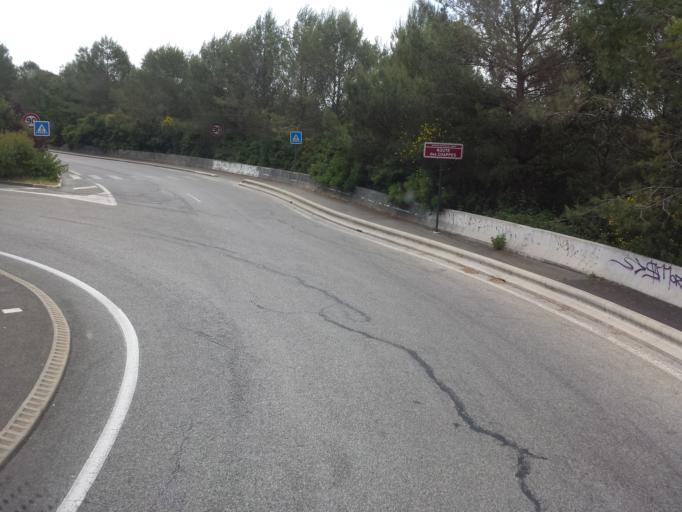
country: FR
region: Provence-Alpes-Cote d'Azur
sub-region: Departement des Alpes-Maritimes
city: Biot
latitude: 43.6120
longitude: 7.0782
